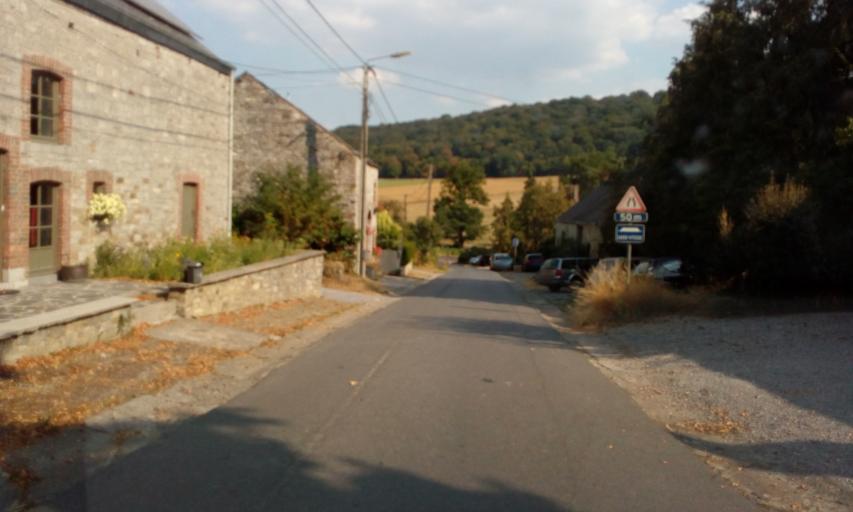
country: BE
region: Wallonia
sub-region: Province du Luxembourg
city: Tellin
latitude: 50.1123
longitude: 5.1672
